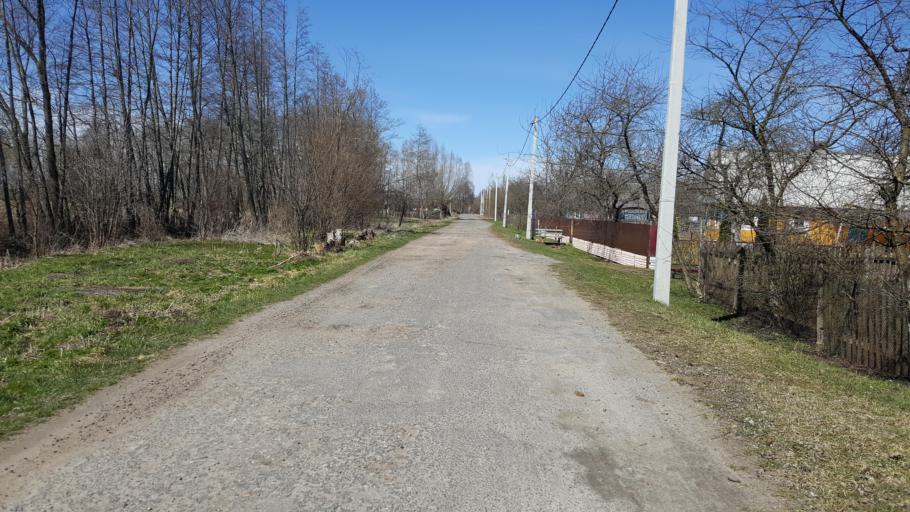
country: BY
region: Brest
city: Zhabinka
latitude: 52.2687
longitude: 23.9404
